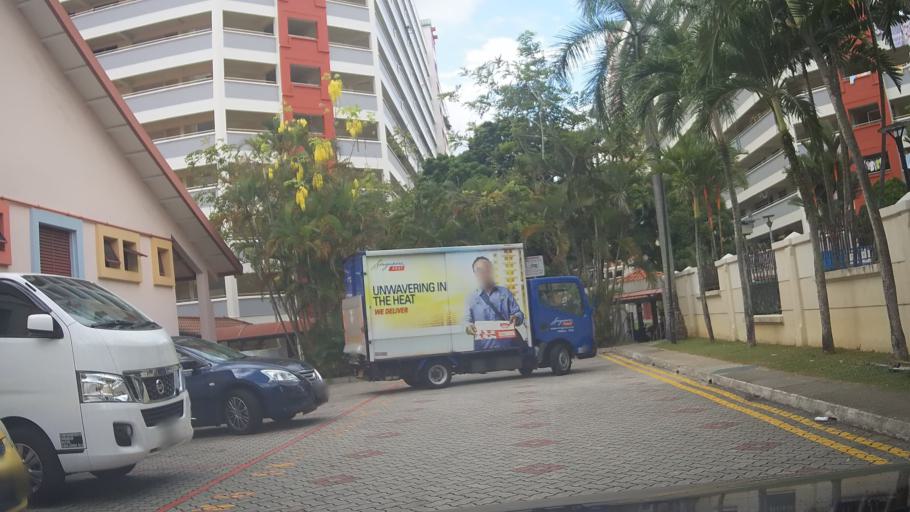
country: MY
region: Johor
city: Johor Bahru
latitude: 1.4432
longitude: 103.7904
